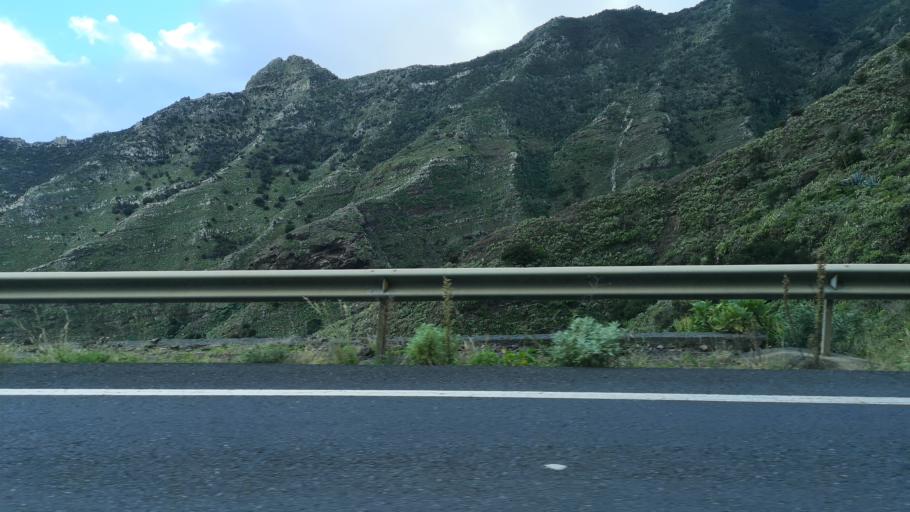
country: ES
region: Canary Islands
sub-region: Provincia de Santa Cruz de Tenerife
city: Hermigua
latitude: 28.1307
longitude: -17.1850
